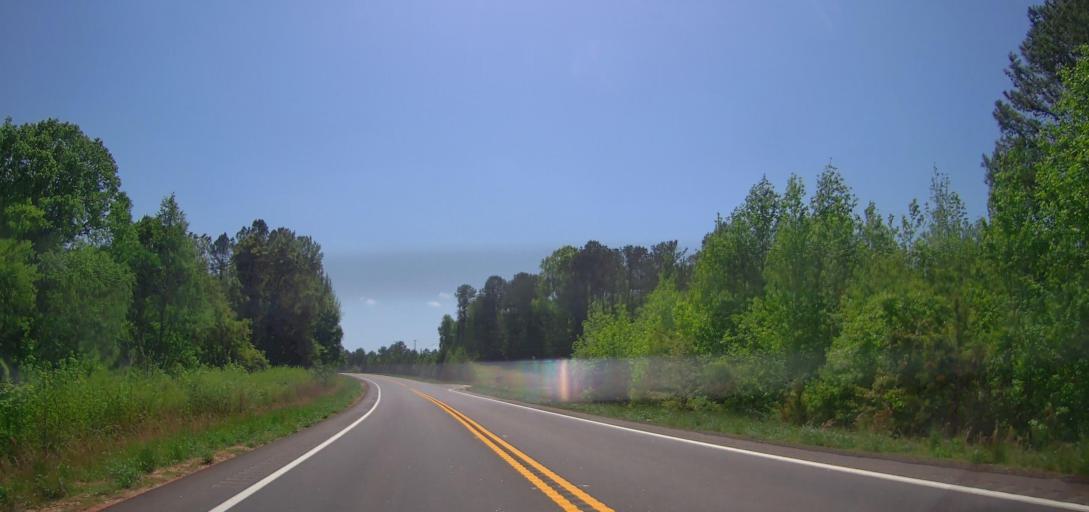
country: US
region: Georgia
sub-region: Putnam County
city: Eatonton
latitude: 33.2554
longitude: -83.4260
